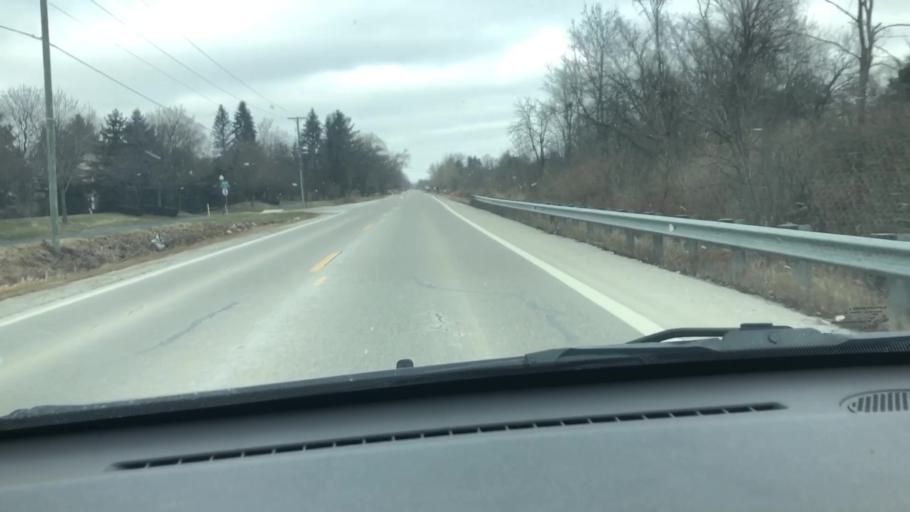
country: US
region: Michigan
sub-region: Macomb County
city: Shelby
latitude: 42.7342
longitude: -83.0171
